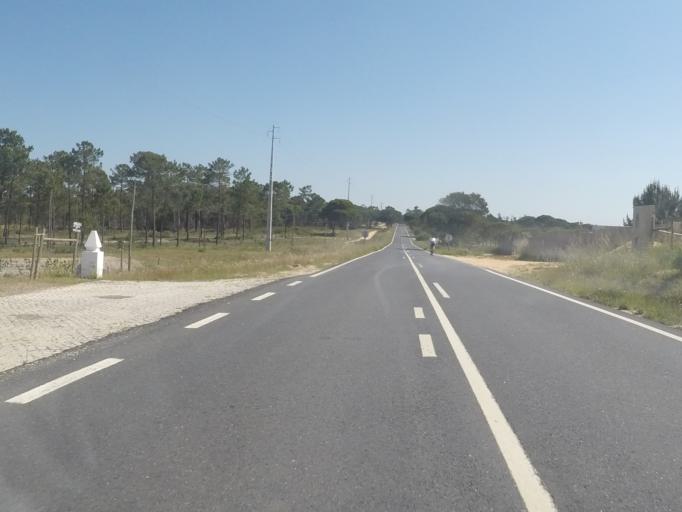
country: PT
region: Setubal
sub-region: Grandola
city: Grandola
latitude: 38.2572
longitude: -8.7360
